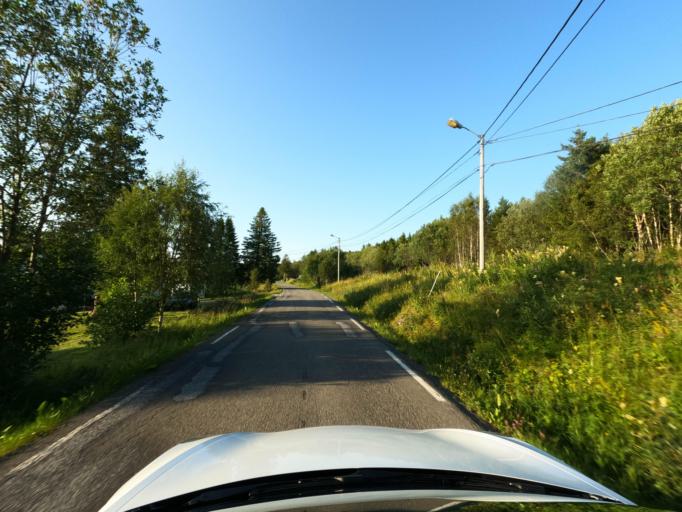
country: NO
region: Nordland
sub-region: Ballangen
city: Ballangen
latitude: 68.4970
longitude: 16.7366
